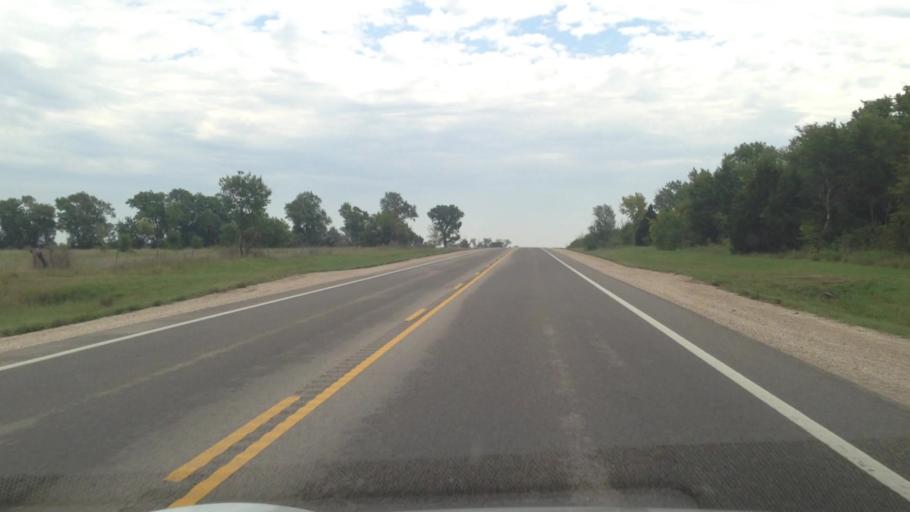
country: US
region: Kansas
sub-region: Allen County
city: Iola
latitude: 37.9088
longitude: -95.1094
